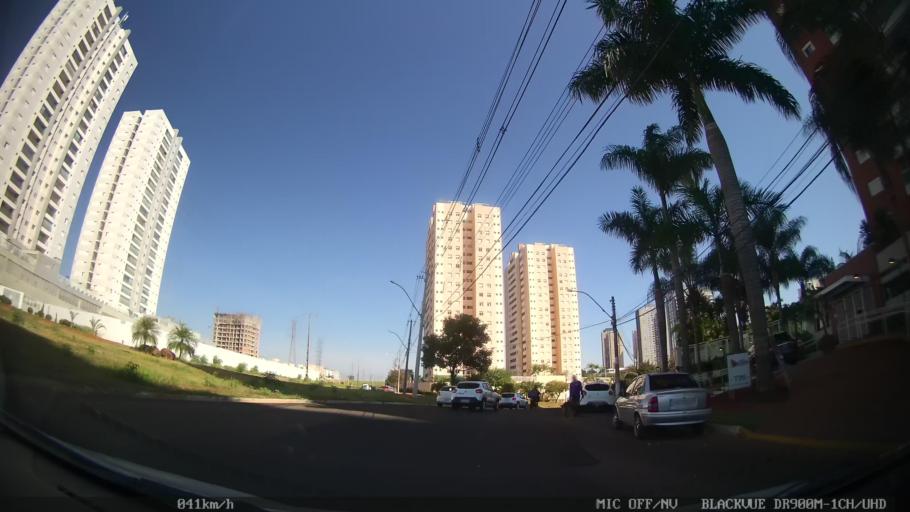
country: BR
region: Sao Paulo
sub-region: Ribeirao Preto
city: Ribeirao Preto
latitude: -21.2196
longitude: -47.7951
